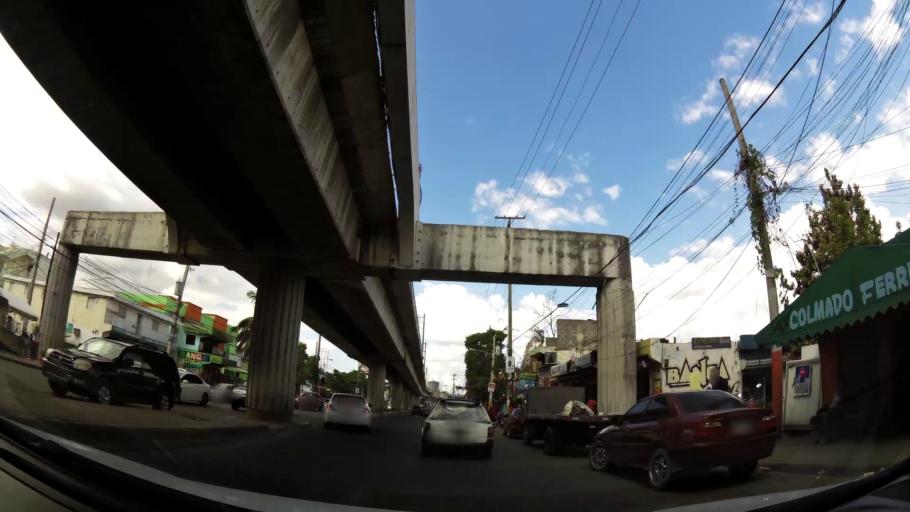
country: DO
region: Nacional
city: Ensanche Luperon
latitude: 18.5403
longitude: -69.9043
